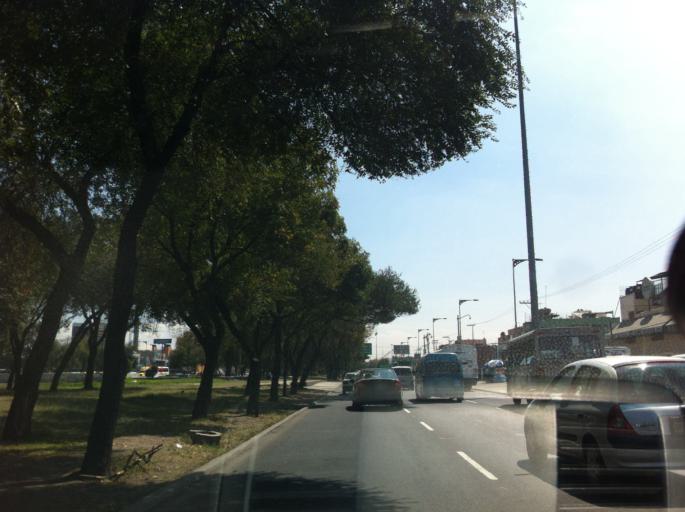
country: MX
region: Mexico City
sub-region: Iztacalco
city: Iztacalco
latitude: 19.4119
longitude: -99.0830
